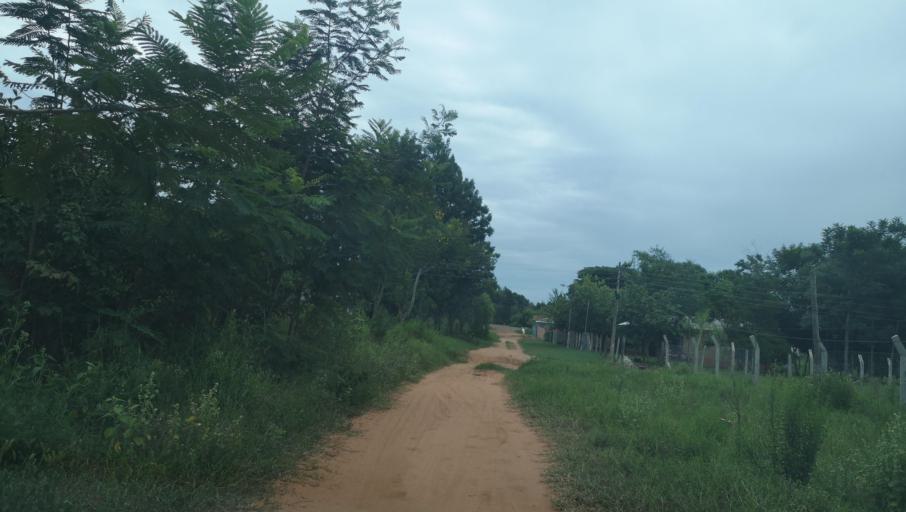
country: PY
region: San Pedro
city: Capiibary
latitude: -24.7384
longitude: -56.0217
